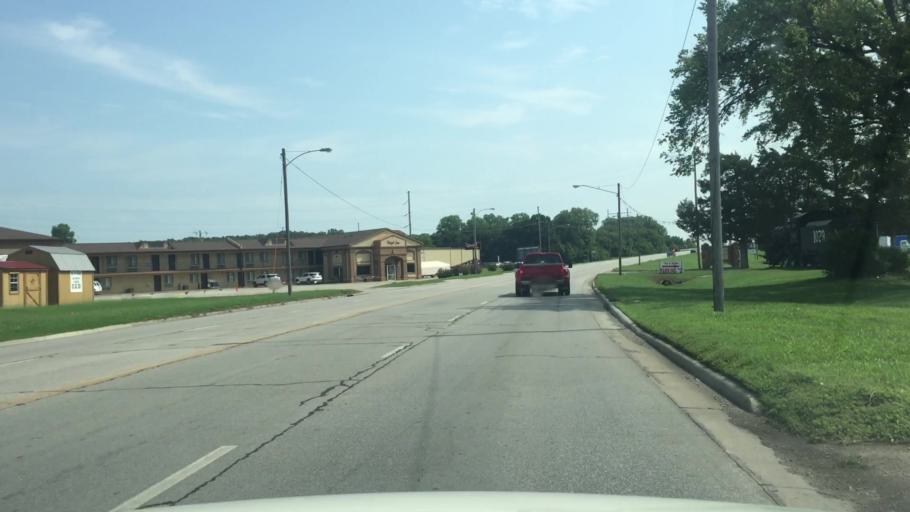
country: US
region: Kansas
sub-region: Montgomery County
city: Coffeyville
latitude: 37.0398
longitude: -95.5966
